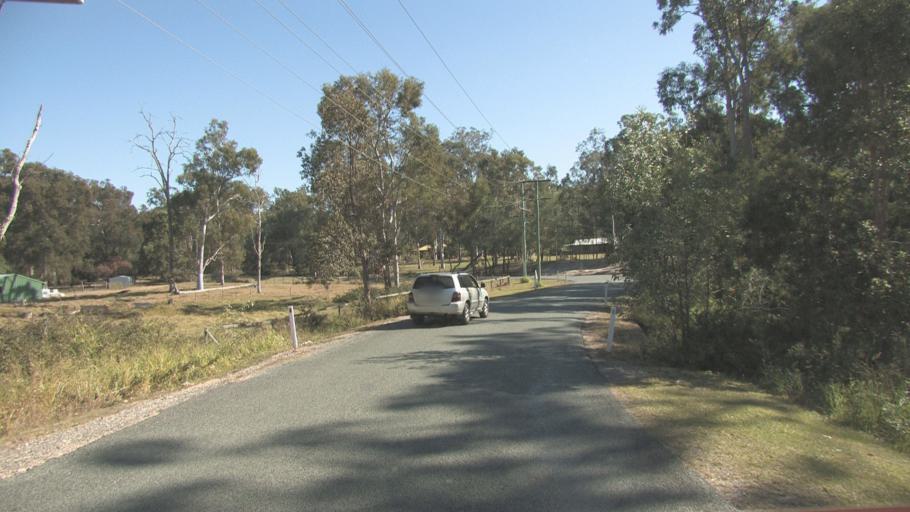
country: AU
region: Queensland
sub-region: Logan
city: Chambers Flat
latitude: -27.7840
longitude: 153.1087
